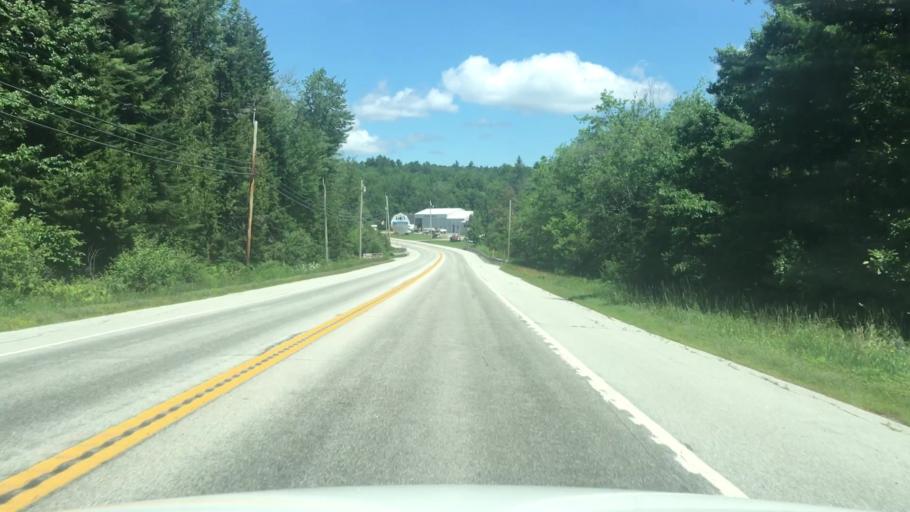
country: US
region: Maine
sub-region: Waldo County
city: Northport
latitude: 44.3516
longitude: -68.9681
